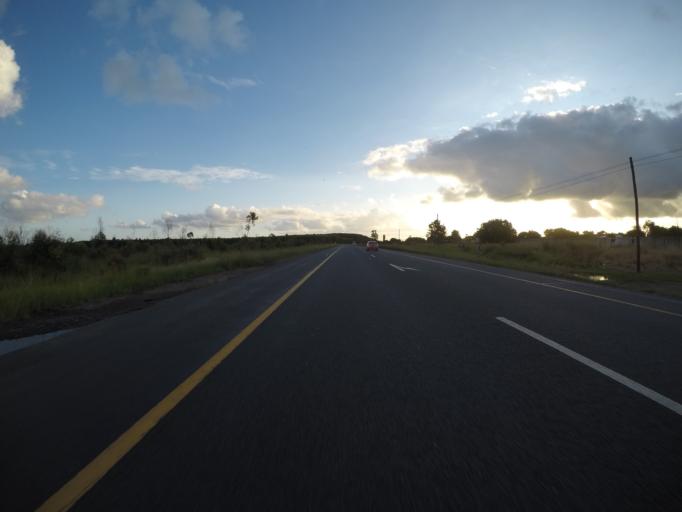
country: ZA
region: KwaZulu-Natal
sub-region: uThungulu District Municipality
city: KwaMbonambi
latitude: -28.6068
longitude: 32.0920
